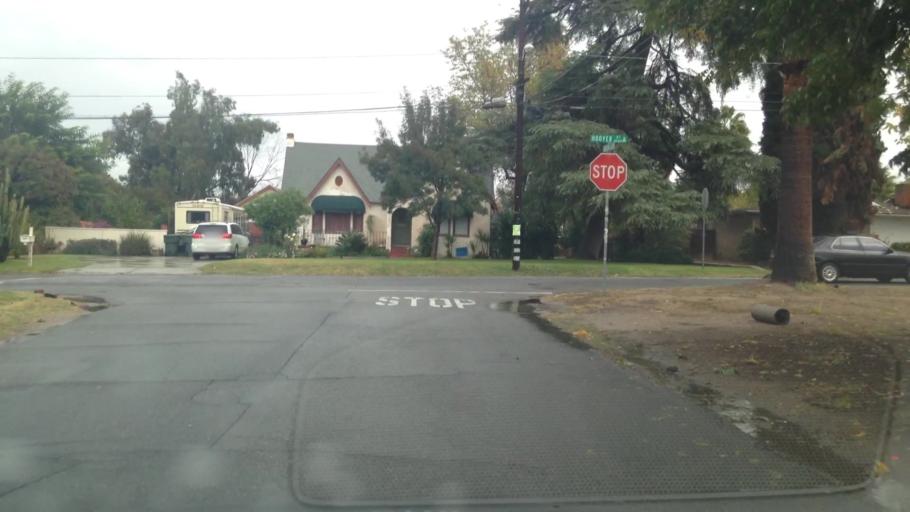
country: US
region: California
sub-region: Riverside County
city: Riverside
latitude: 33.9391
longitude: -117.4031
